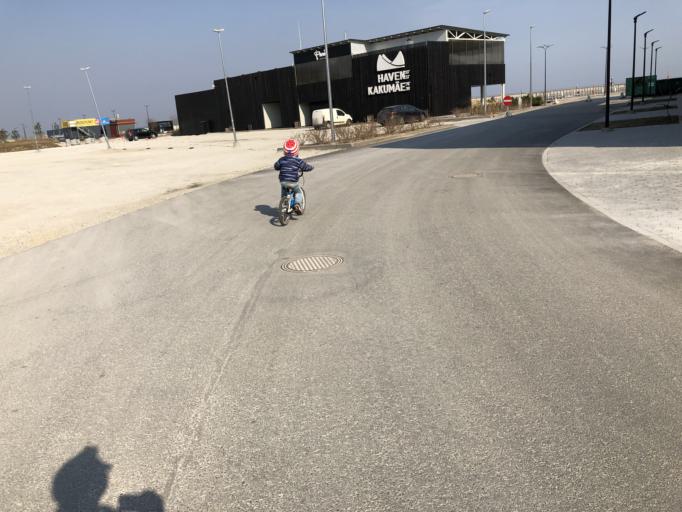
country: EE
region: Harju
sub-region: Harku vald
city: Tabasalu
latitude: 59.4502
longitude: 24.6041
